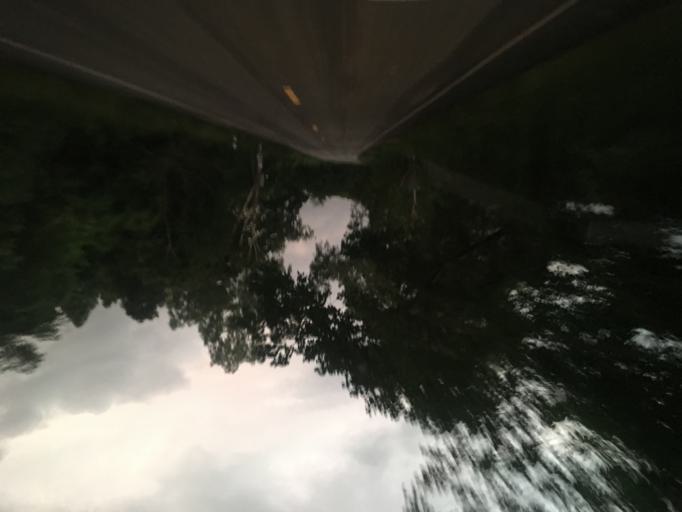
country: TH
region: Changwat Udon Thani
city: Udon Thani
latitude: 17.3519
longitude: 102.7196
